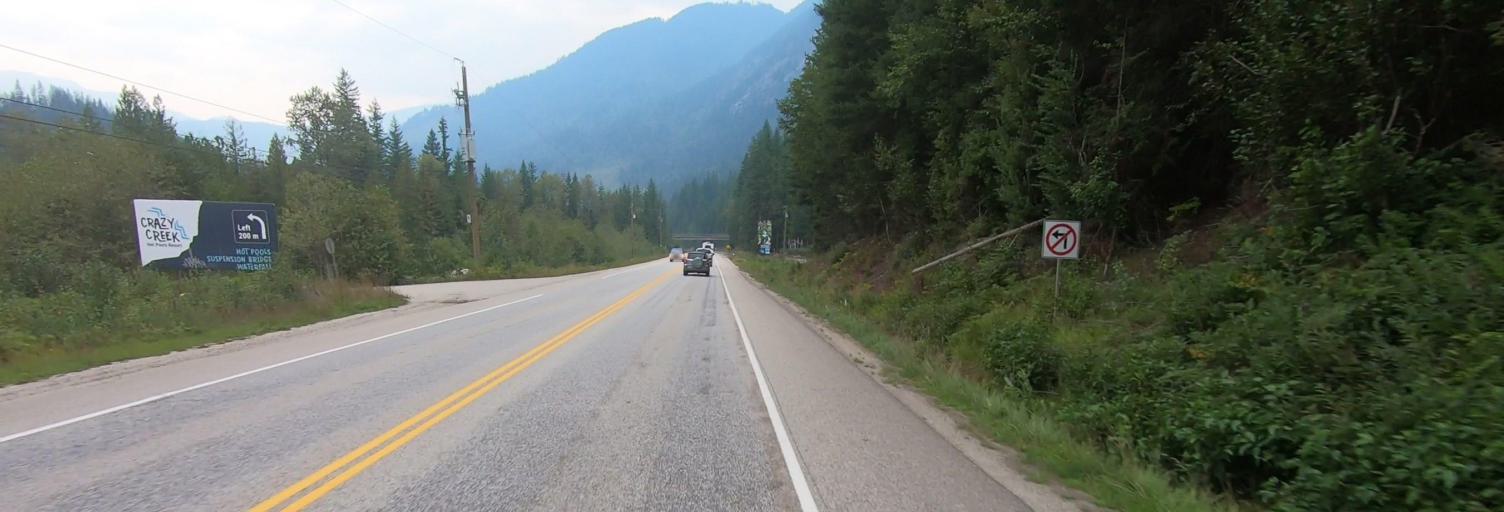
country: CA
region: British Columbia
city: Sicamous
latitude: 50.9939
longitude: -118.6411
